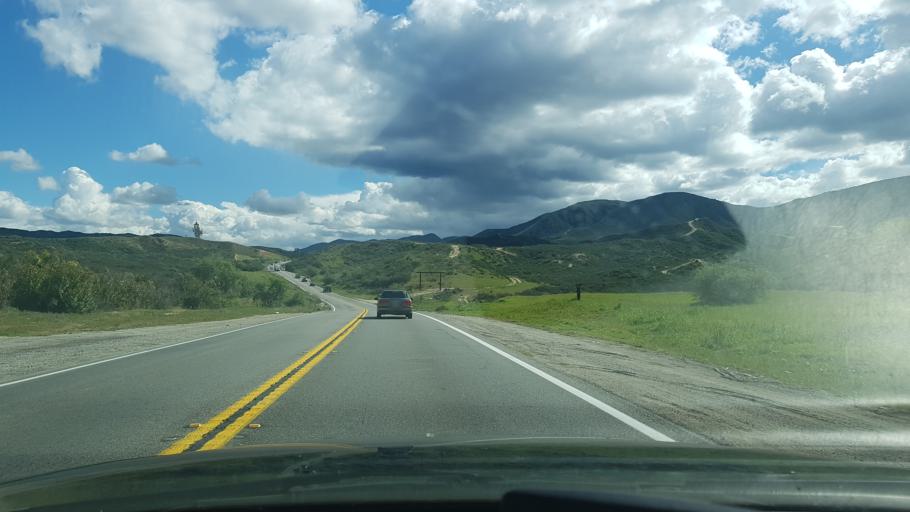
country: US
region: California
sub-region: Riverside County
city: Temecula
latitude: 33.4813
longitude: -117.0389
